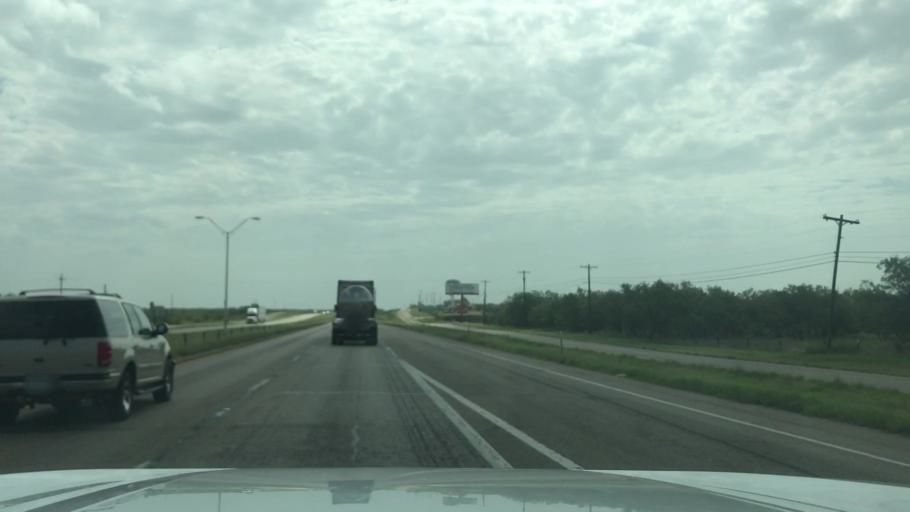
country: US
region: Texas
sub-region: Callahan County
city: Clyde
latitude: 32.4314
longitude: -99.6011
